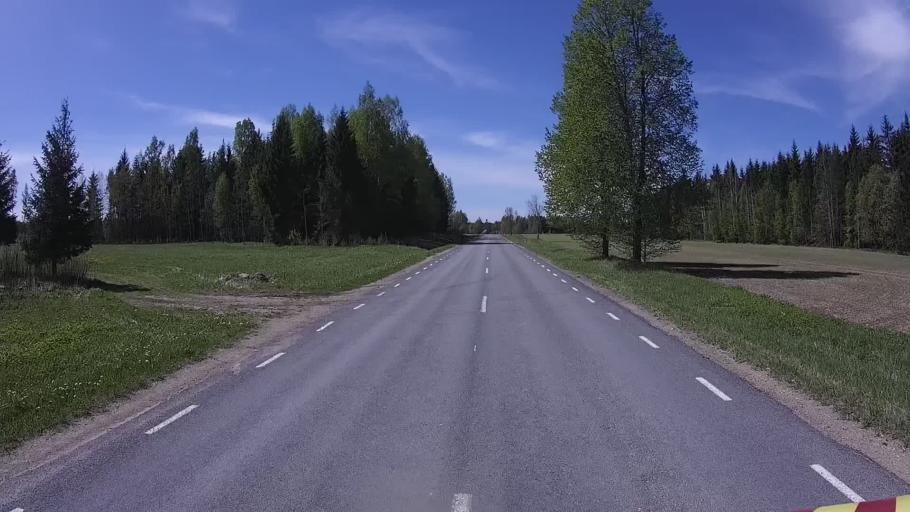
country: EE
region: Polvamaa
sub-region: Raepina vald
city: Rapina
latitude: 57.9798
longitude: 27.3004
